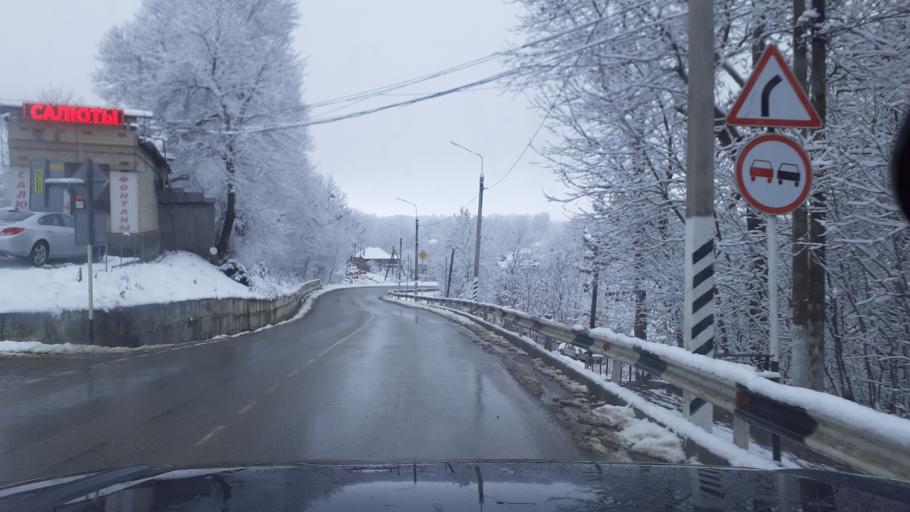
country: RU
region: Adygeya
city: Tul'skiy
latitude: 44.5075
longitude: 40.1752
